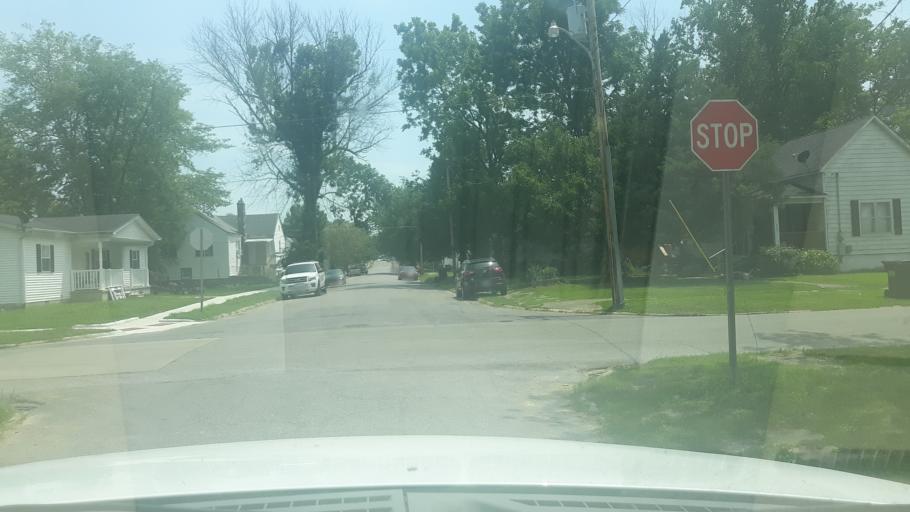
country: US
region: Illinois
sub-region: Saline County
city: Harrisburg
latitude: 37.7332
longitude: -88.5445
